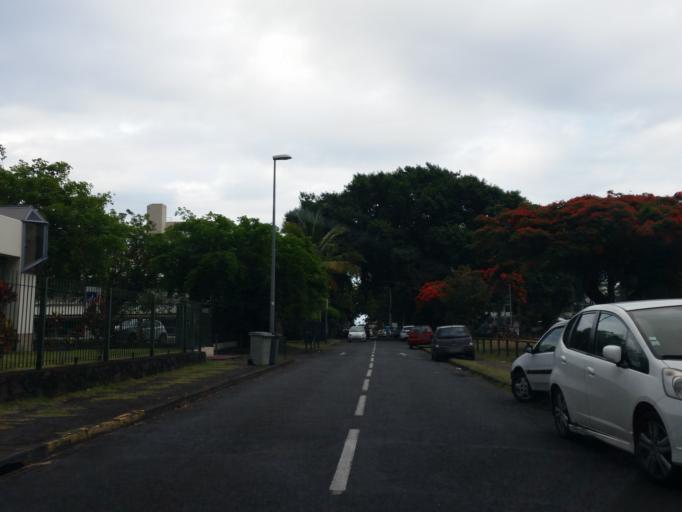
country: RE
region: Reunion
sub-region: Reunion
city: Saint-Denis
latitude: -20.8901
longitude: 55.4658
